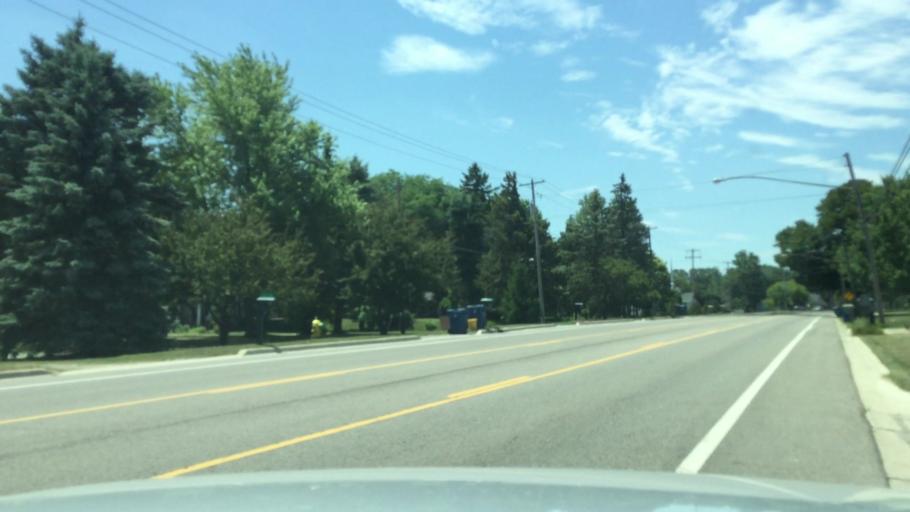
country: US
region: Michigan
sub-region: Genesee County
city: Swartz Creek
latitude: 42.9599
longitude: -83.8196
